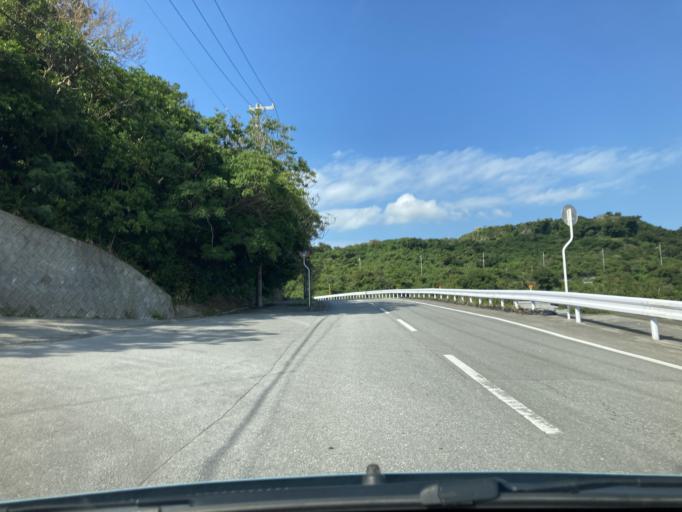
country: JP
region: Okinawa
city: Chatan
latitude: 26.2800
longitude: 127.7992
